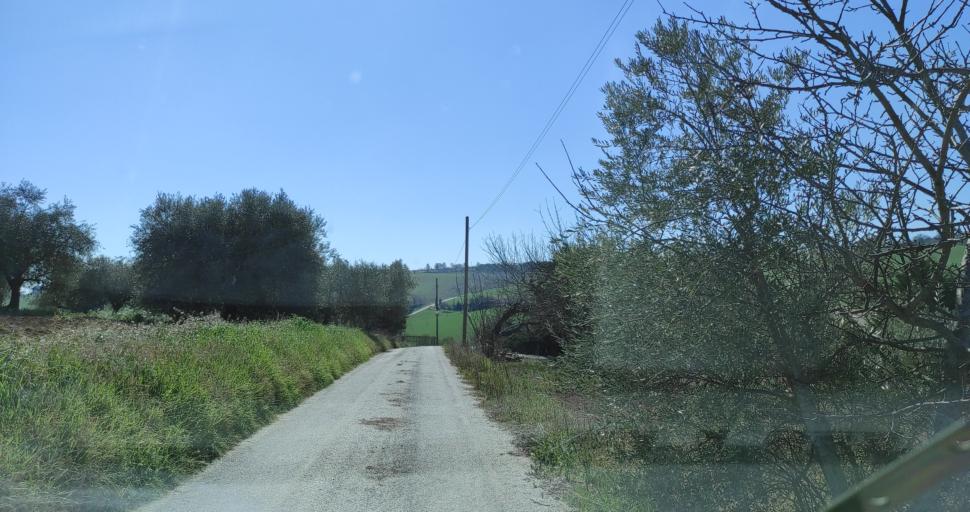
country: IT
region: The Marches
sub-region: Provincia di Macerata
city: Piediripa
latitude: 43.3119
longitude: 13.5028
